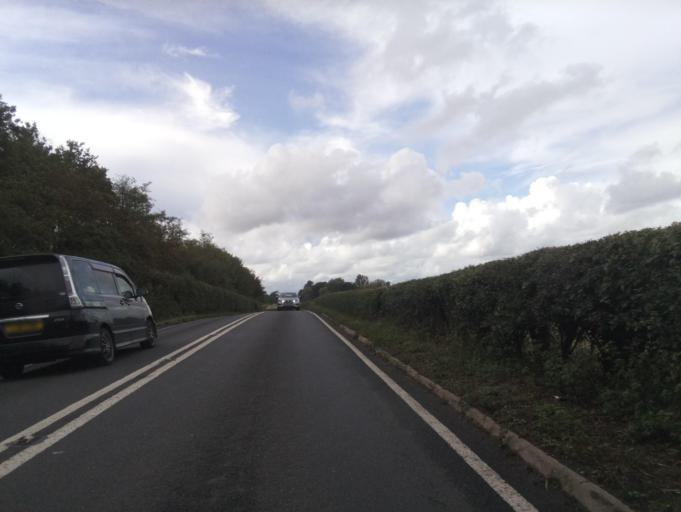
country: GB
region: England
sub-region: Worcestershire
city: Droitwich
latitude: 52.3373
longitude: -2.1863
